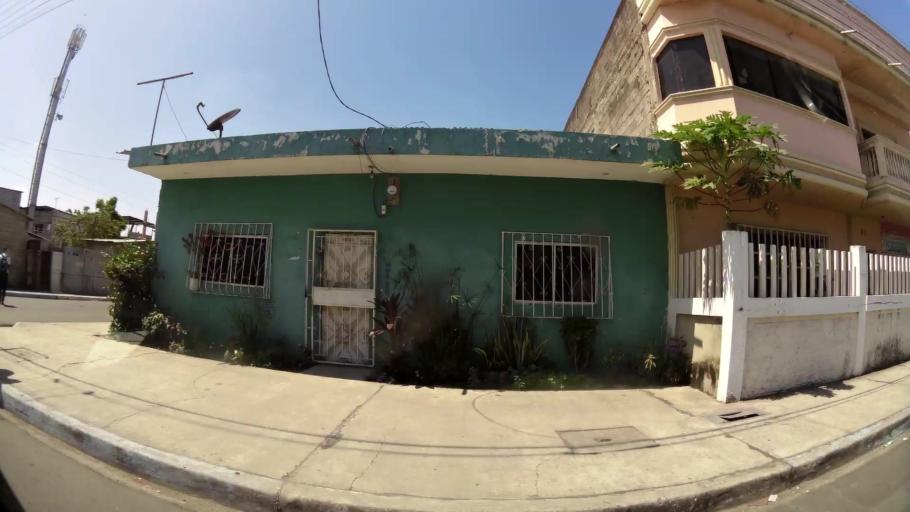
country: EC
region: Guayas
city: Guayaquil
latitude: -2.2345
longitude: -79.9196
